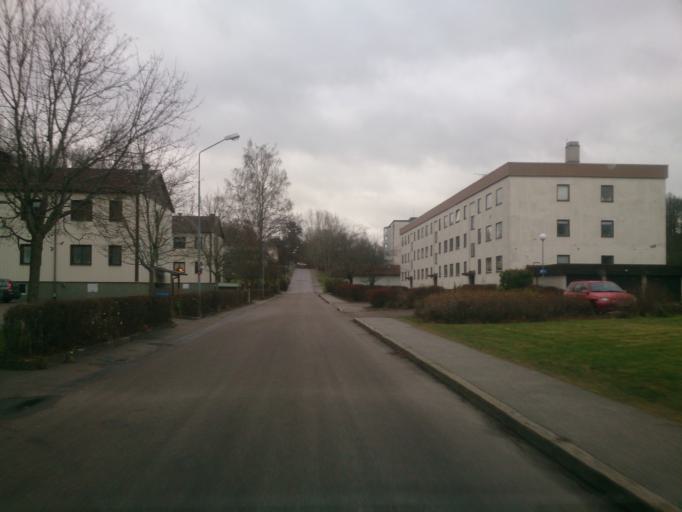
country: SE
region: OEstergoetland
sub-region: Atvidabergs Kommun
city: Atvidaberg
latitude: 58.1951
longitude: 16.0021
